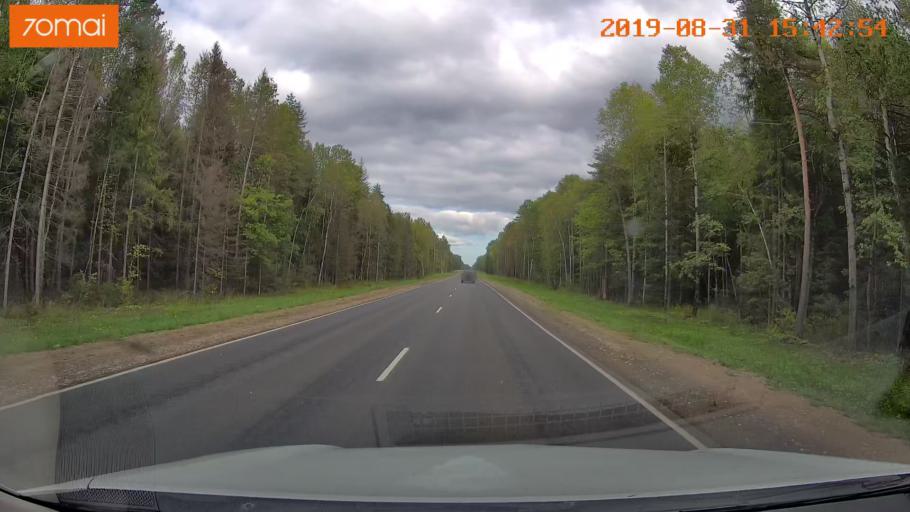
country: RU
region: Kaluga
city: Mosal'sk
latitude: 54.6494
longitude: 34.8975
